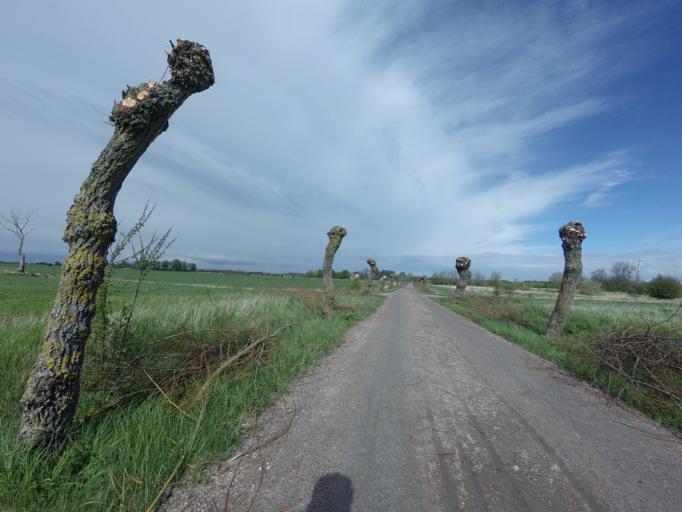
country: SE
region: Skane
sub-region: Malmo
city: Bunkeflostrand
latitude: 55.5422
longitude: 12.9702
